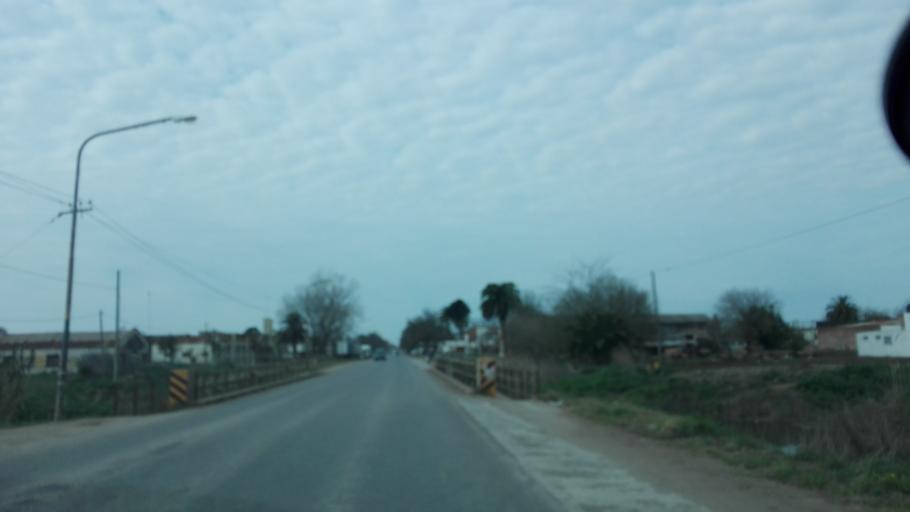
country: AR
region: Buenos Aires
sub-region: Partido de Chascomus
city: Chascomus
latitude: -35.5753
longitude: -57.9943
